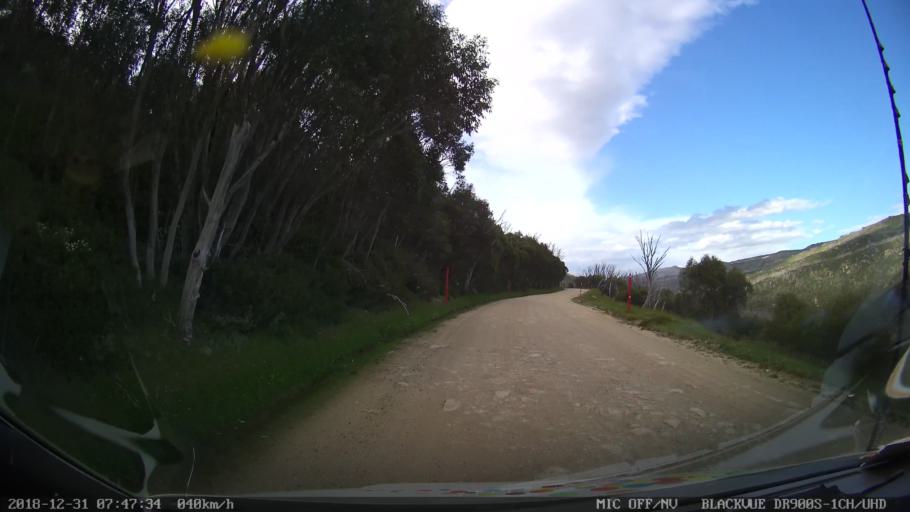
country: AU
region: New South Wales
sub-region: Snowy River
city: Jindabyne
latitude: -36.3645
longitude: 148.3955
